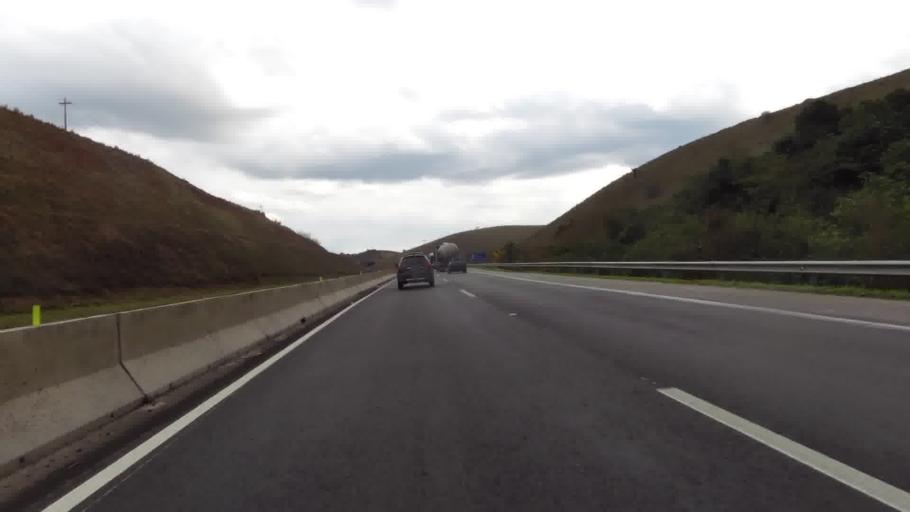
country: BR
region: Rio de Janeiro
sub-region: Casimiro De Abreu
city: Casimiro de Abreu
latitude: -22.4678
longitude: -42.0742
